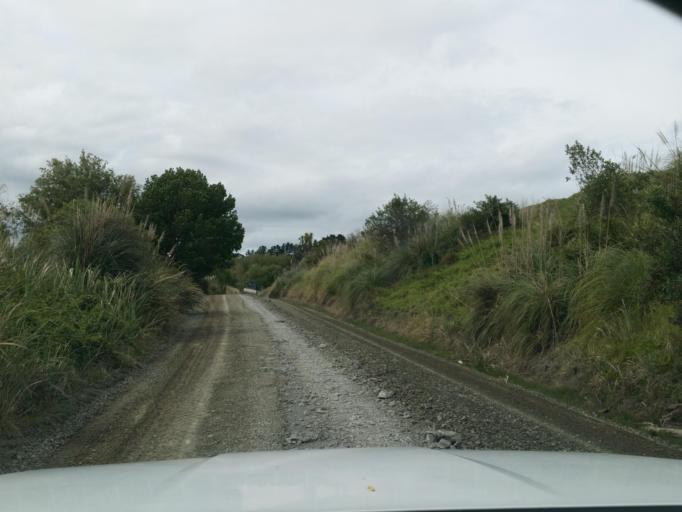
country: NZ
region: Northland
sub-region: Kaipara District
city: Dargaville
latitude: -35.9144
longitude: 173.9201
